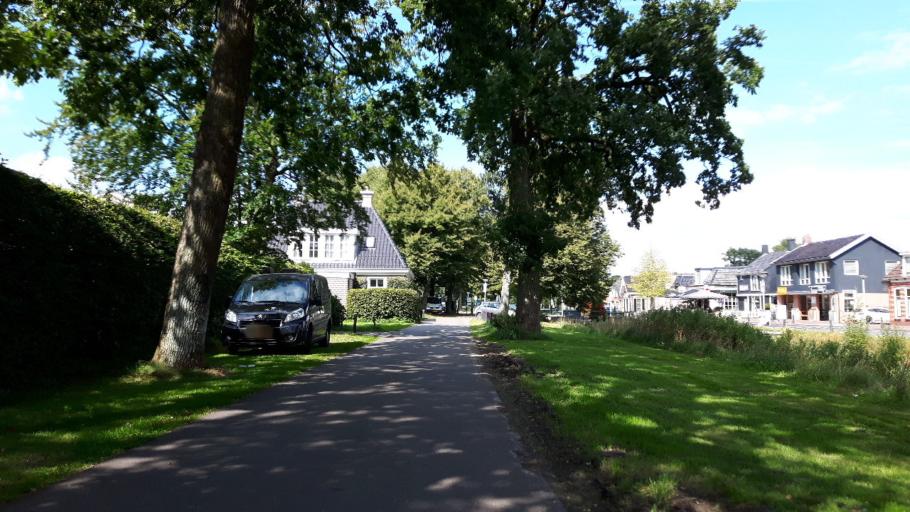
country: NL
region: Friesland
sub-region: Gemeente Smallingerland
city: Drachtstercompagnie
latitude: 53.0799
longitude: 6.2571
